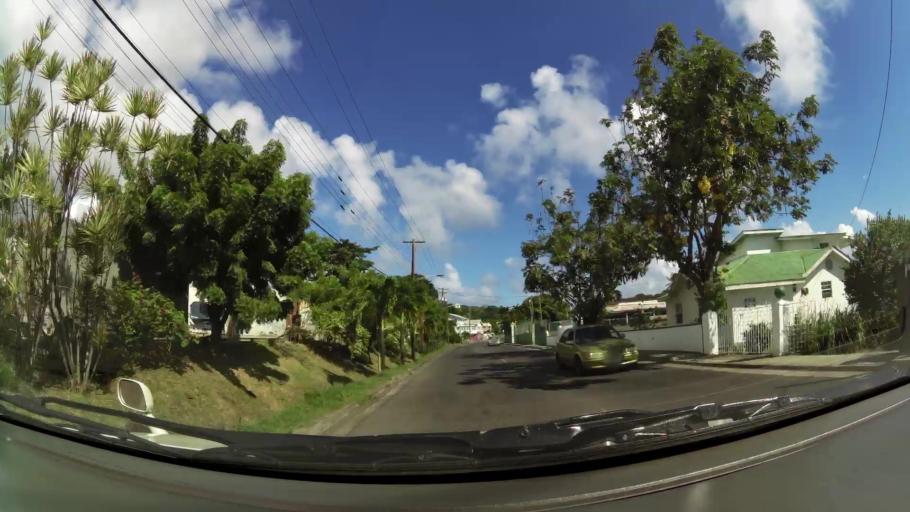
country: VC
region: Saint George
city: Kingstown
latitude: 13.1319
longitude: -61.1978
